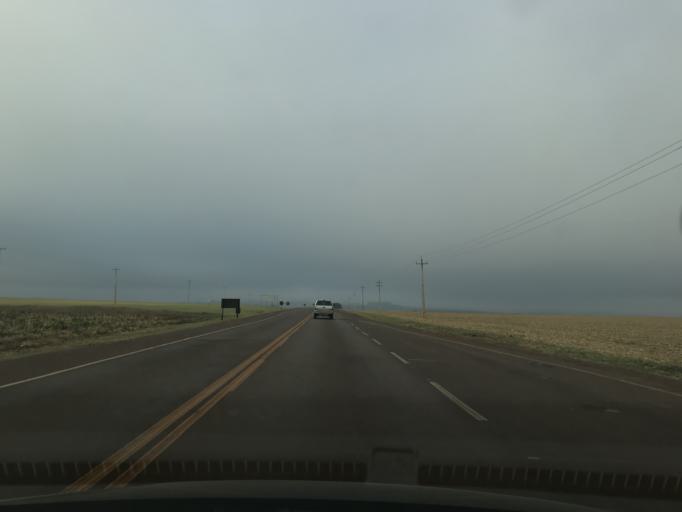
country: BR
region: Parana
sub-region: Toledo
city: Toledo
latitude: -24.6192
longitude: -53.7126
